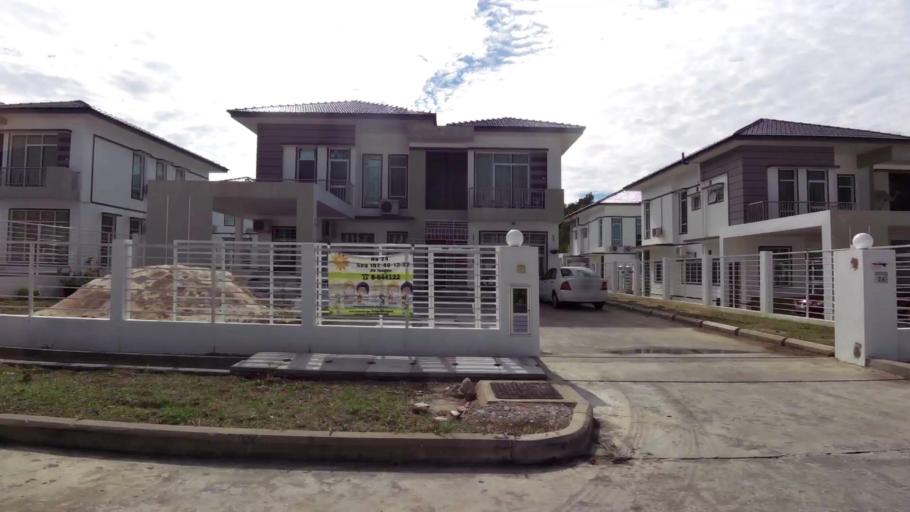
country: BN
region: Brunei and Muara
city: Bandar Seri Begawan
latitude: 4.9246
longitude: 114.8984
